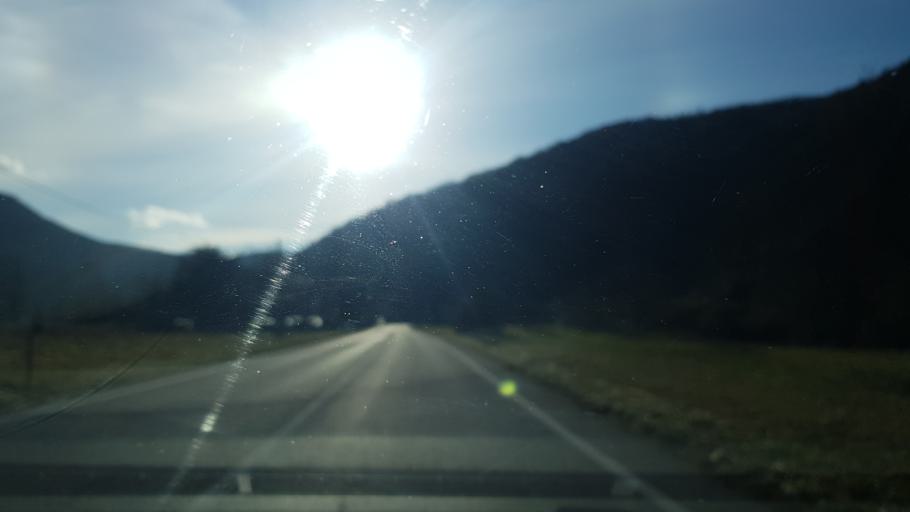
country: IT
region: Friuli Venezia Giulia
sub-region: Provincia di Udine
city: Merso di Sopra
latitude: 46.1272
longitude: 13.5268
